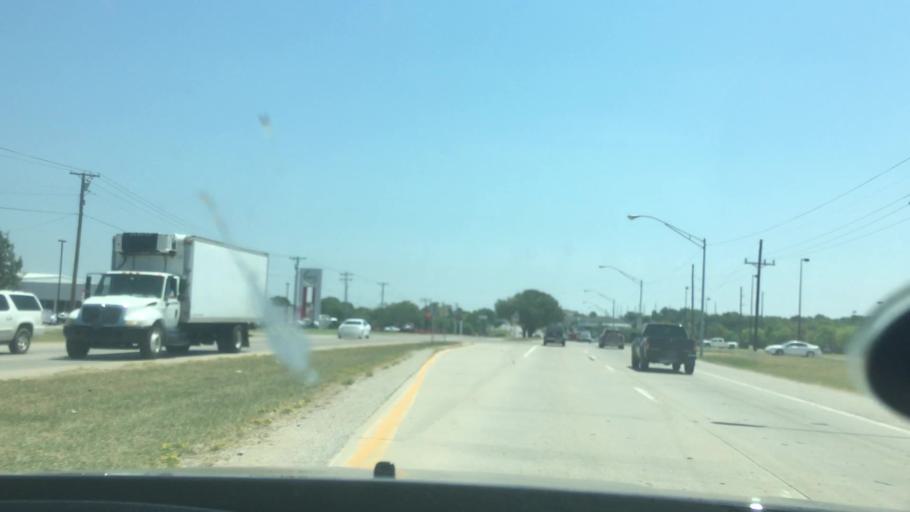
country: US
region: Oklahoma
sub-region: Pontotoc County
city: Ada
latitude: 34.7897
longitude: -96.6738
